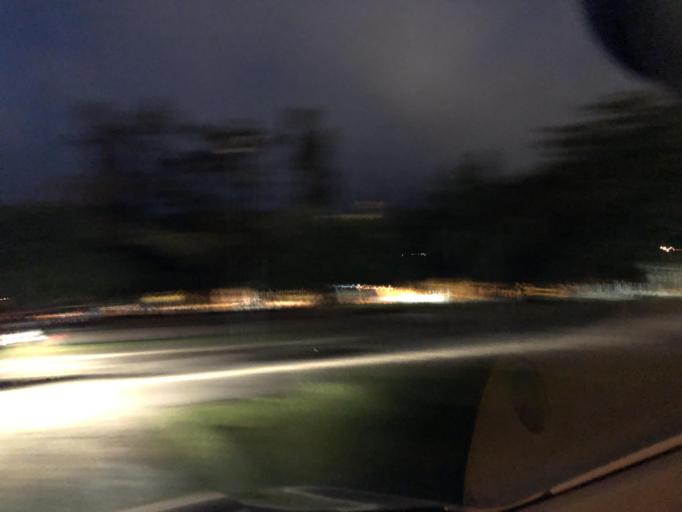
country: BR
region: Santa Catarina
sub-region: Florianopolis
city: Carvoeira
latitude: -27.5987
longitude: -48.5188
